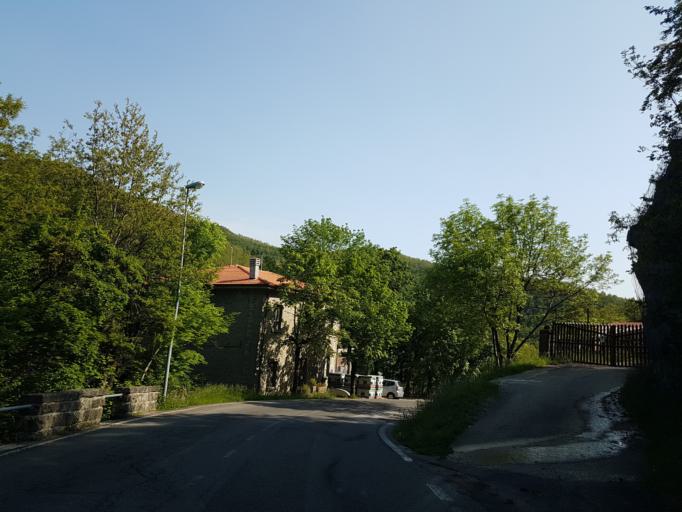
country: IT
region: Tuscany
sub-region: Province of Arezzo
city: Soci
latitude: 43.7911
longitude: 11.8776
